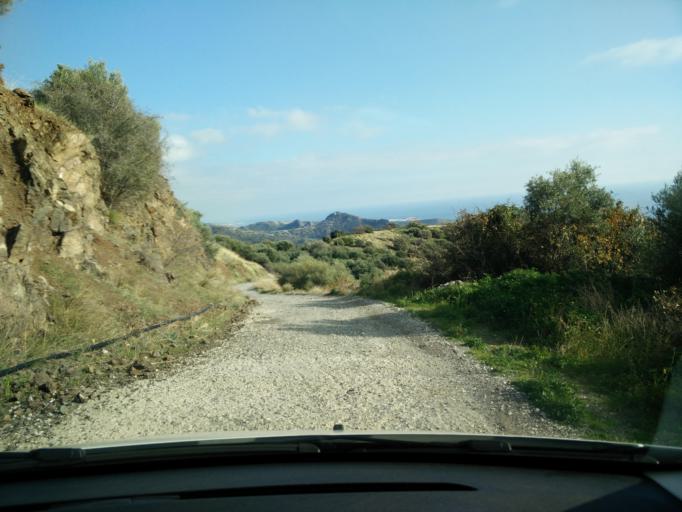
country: GR
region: Crete
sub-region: Nomos Lasithiou
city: Gra Liyia
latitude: 35.0322
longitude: 25.5675
